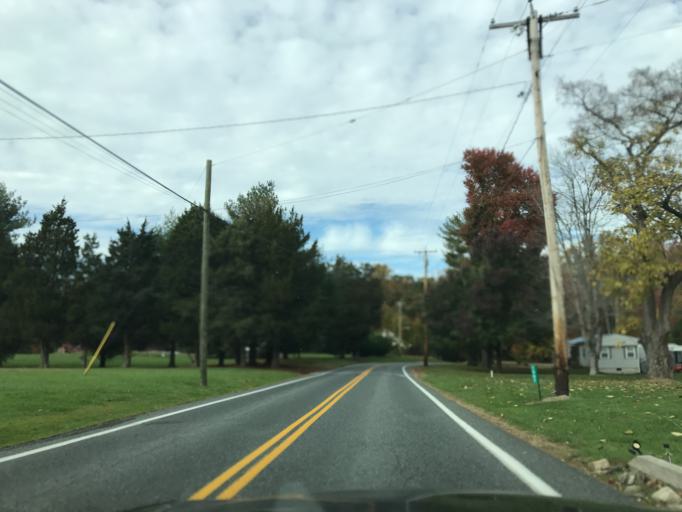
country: US
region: Maryland
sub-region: Harford County
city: Joppatowne
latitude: 39.4361
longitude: -76.3629
